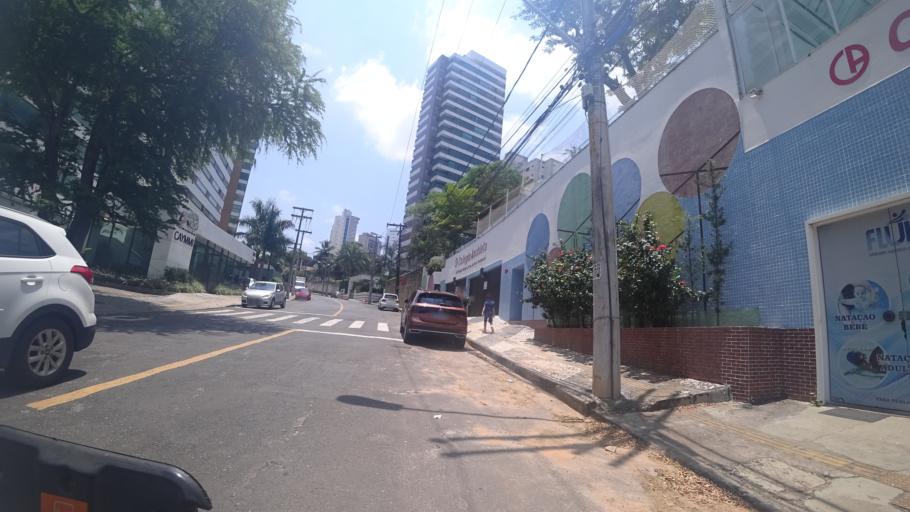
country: BR
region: Bahia
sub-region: Salvador
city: Salvador
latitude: -12.9897
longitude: -38.4537
